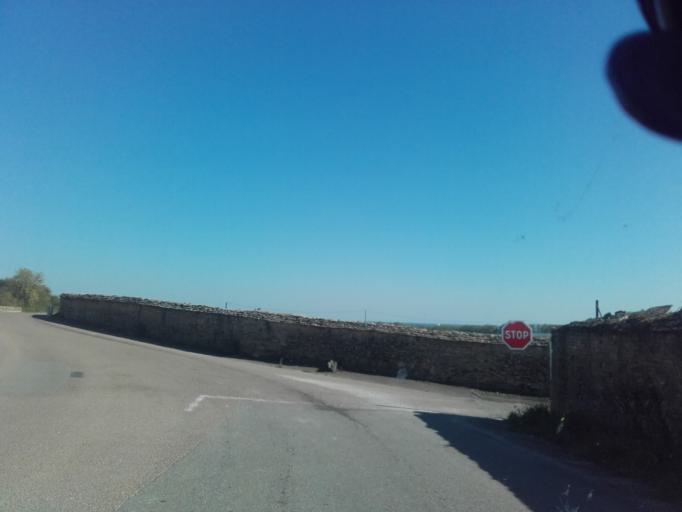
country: FR
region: Bourgogne
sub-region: Departement de la Cote-d'Or
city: Bligny-les-Beaune
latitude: 47.0127
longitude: 4.7951
